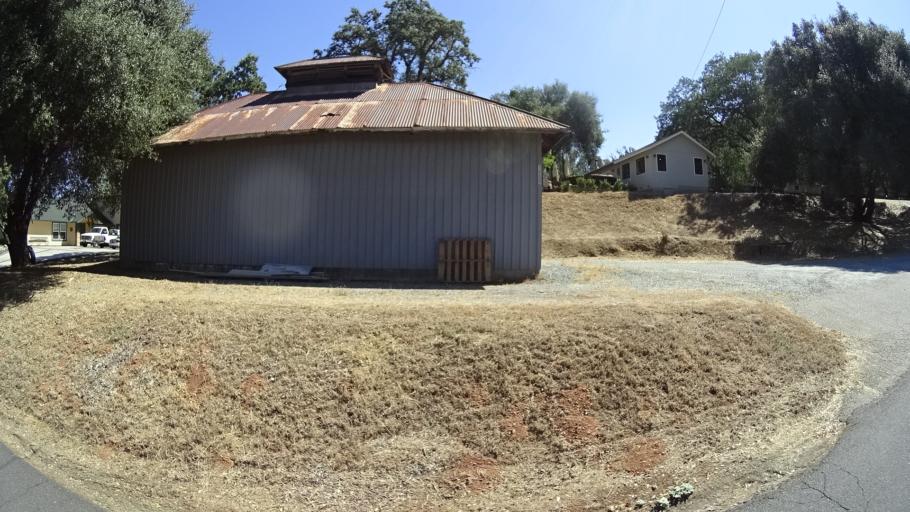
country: US
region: California
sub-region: Calaveras County
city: Angels Camp
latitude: 38.0598
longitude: -120.5396
